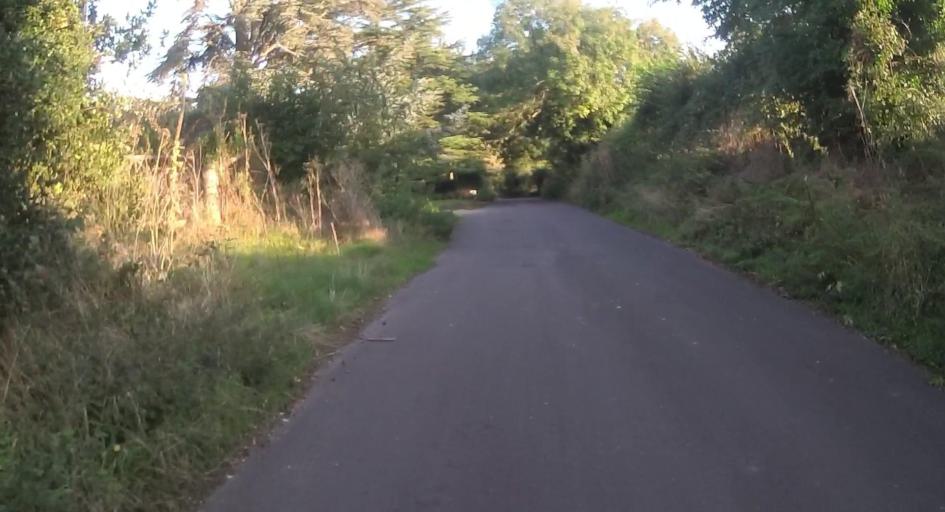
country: GB
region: England
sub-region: Hampshire
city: Old Basing
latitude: 51.2589
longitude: -1.0196
